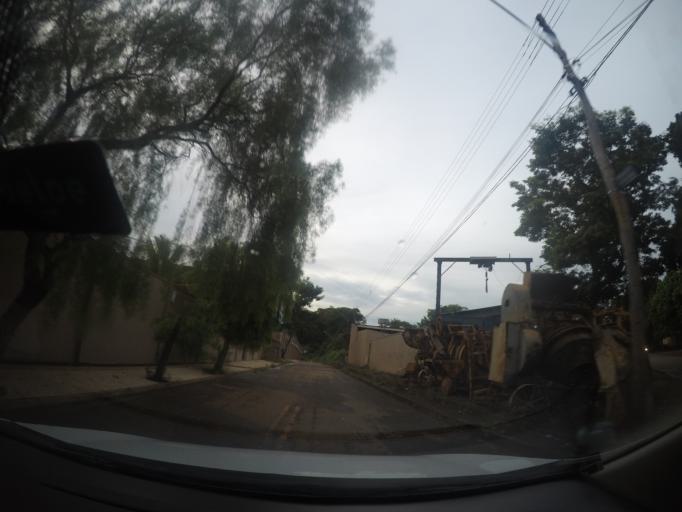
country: BR
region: Goias
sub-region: Goiania
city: Goiania
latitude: -16.6336
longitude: -49.2398
